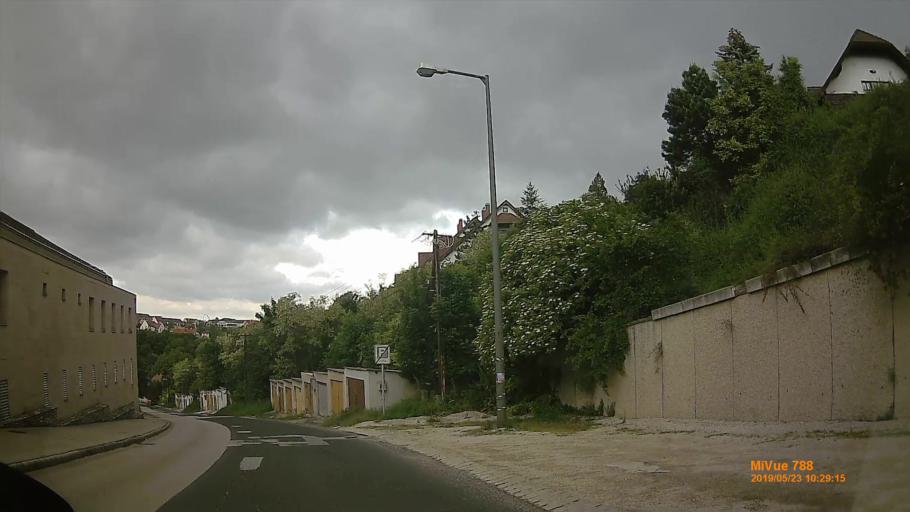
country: HU
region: Veszprem
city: Veszprem
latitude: 47.0979
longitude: 17.9114
